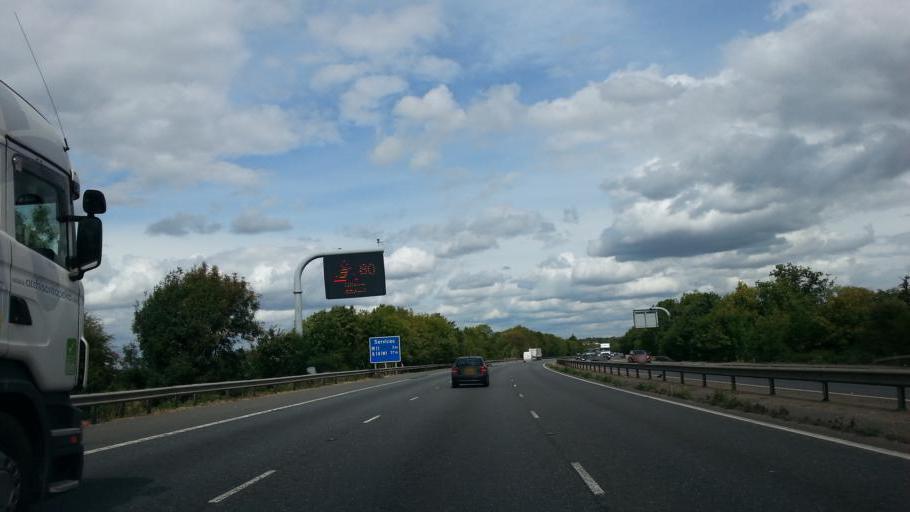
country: GB
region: England
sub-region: Essex
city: Little Hallingbury
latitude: 51.8250
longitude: 0.1863
